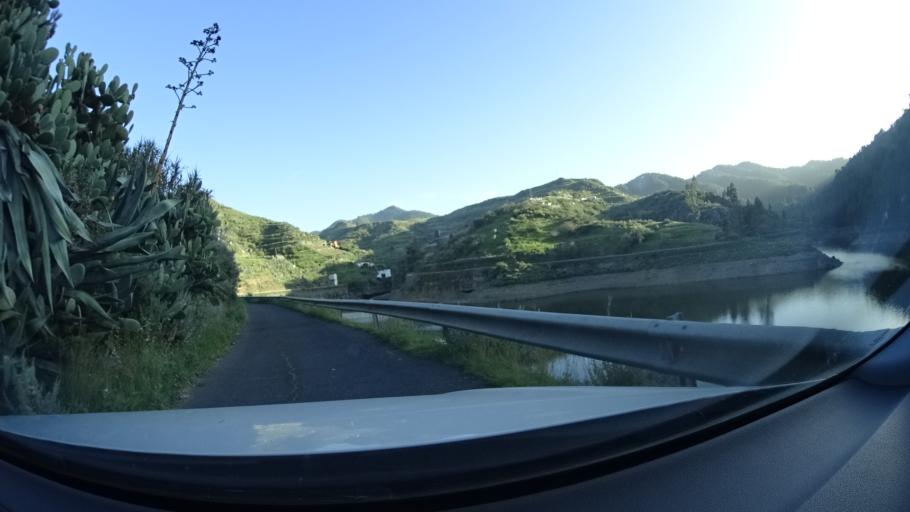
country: ES
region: Canary Islands
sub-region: Provincia de Las Palmas
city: Artenara
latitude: 28.0462
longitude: -15.6725
